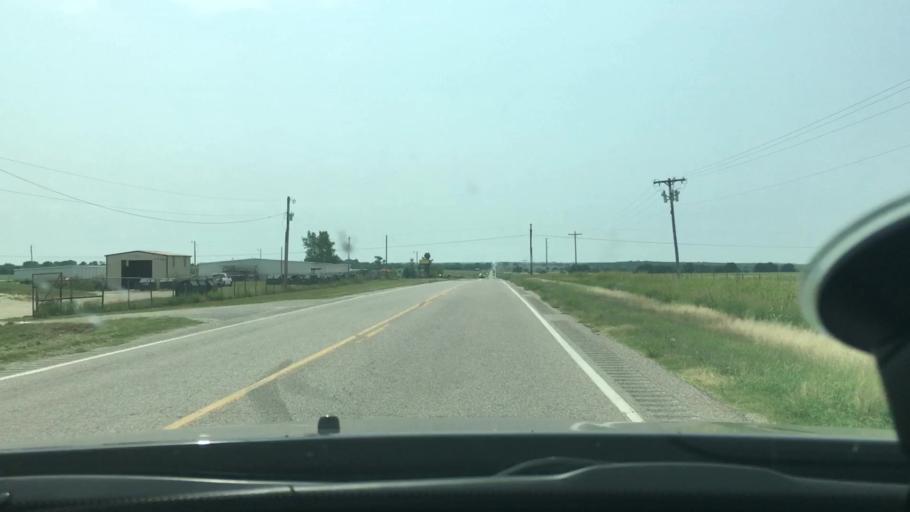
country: US
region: Oklahoma
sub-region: Marshall County
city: Kingston
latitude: 34.0128
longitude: -96.7611
